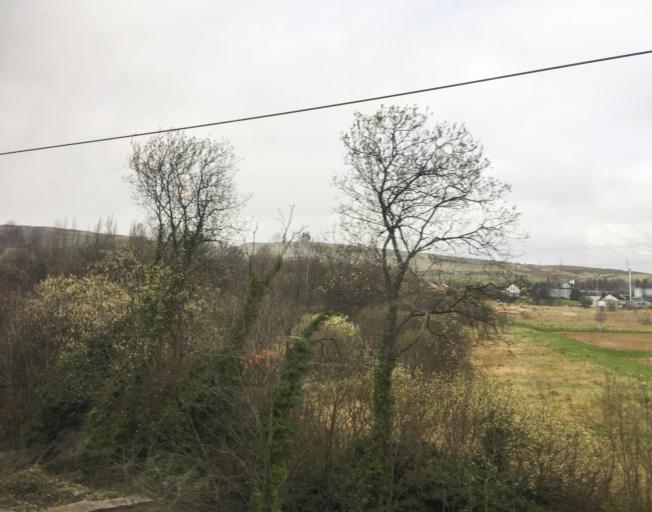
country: GB
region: Scotland
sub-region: West Dunbartonshire
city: Old Kilpatrick
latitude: 55.9184
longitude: -4.4421
